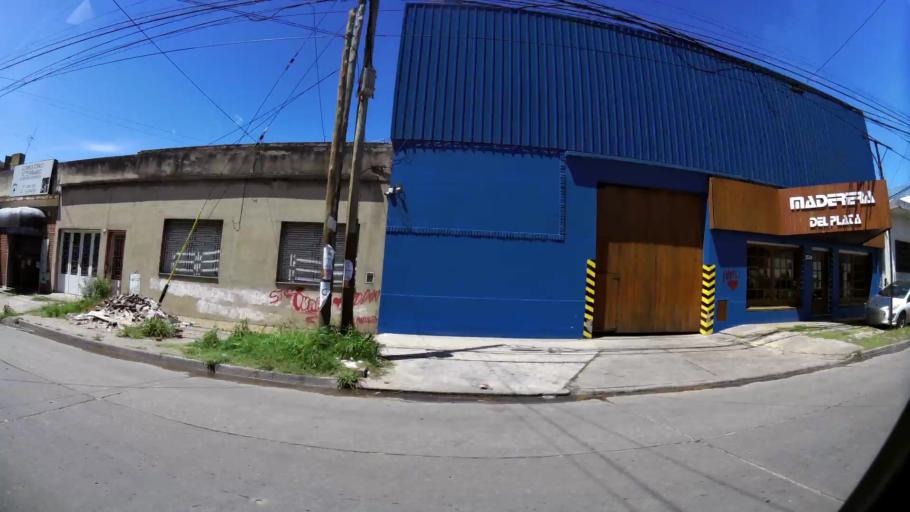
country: AR
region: Buenos Aires
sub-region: Partido de Quilmes
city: Quilmes
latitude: -34.7398
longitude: -58.2843
